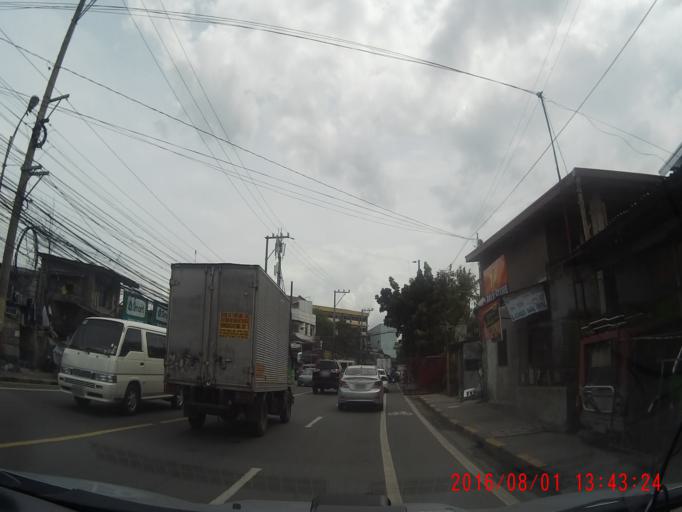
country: PH
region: Metro Manila
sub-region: Pasig
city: Pasig City
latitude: 14.5677
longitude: 121.0806
